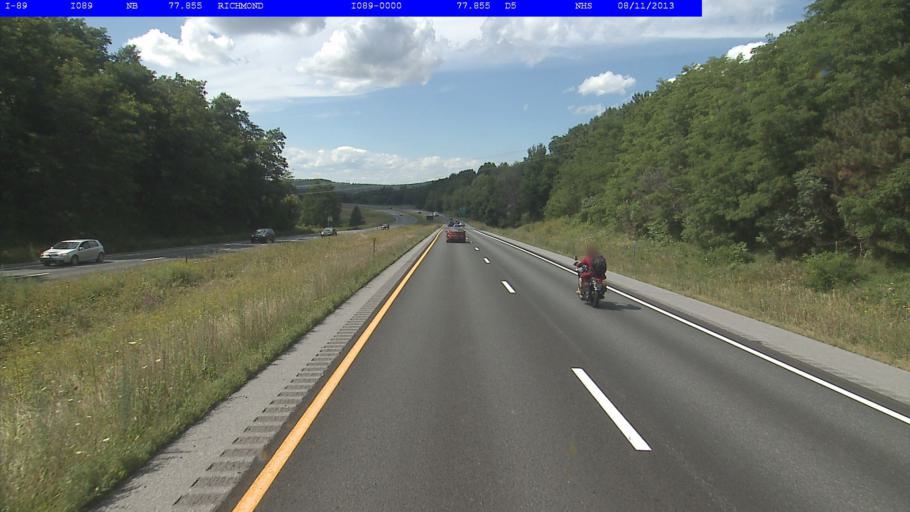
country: US
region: Vermont
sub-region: Chittenden County
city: Williston
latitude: 44.4206
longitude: -73.0014
